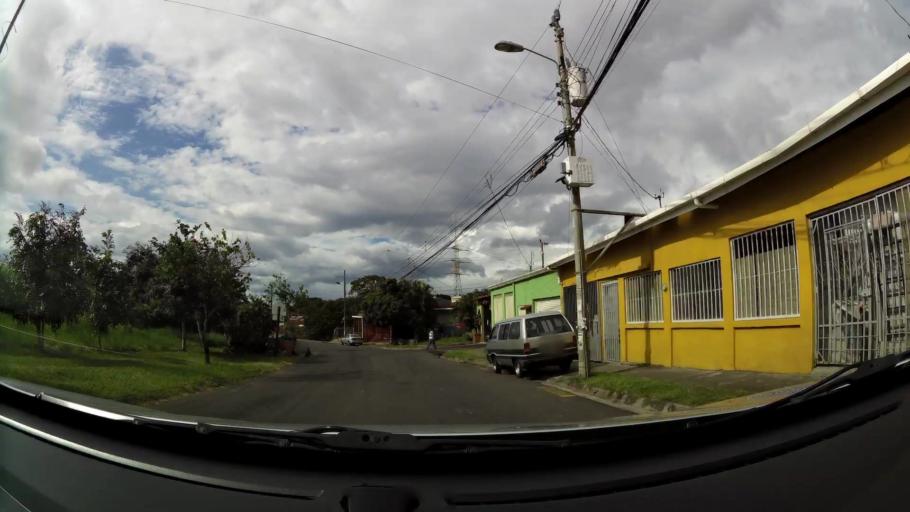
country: CR
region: San Jose
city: San Rafael
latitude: 9.9567
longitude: -84.1280
